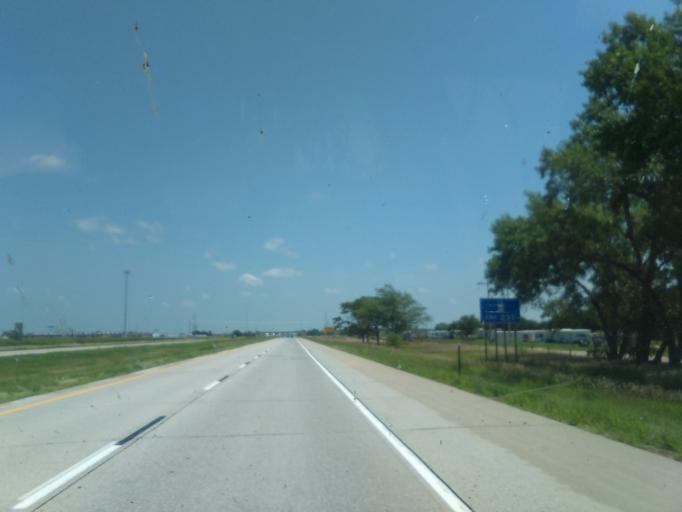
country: US
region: Nebraska
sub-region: Dawson County
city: Lexington
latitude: 40.7447
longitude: -99.7542
